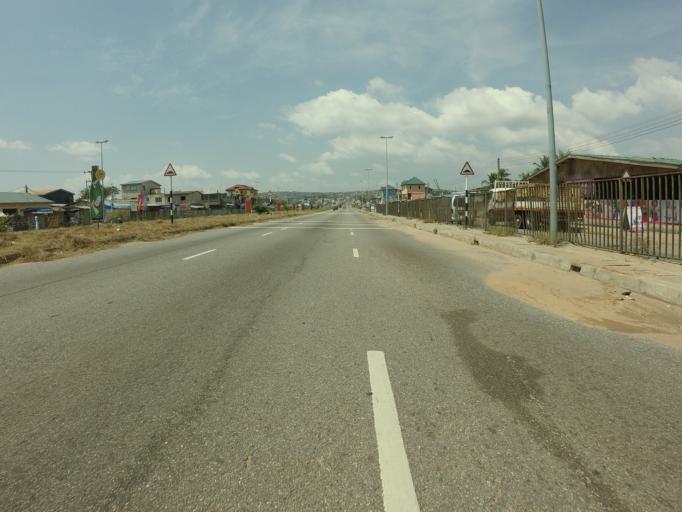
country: GH
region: Greater Accra
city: Gbawe
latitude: 5.5865
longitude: -0.2780
